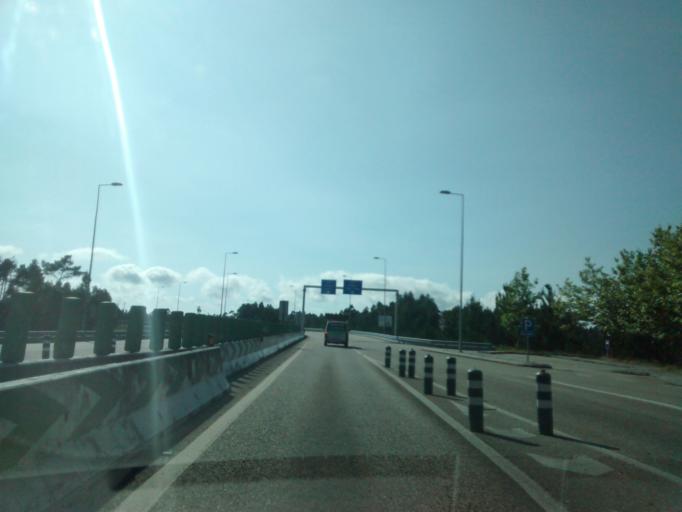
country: PT
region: Leiria
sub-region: Pombal
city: Lourical
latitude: 39.9895
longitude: -8.7916
